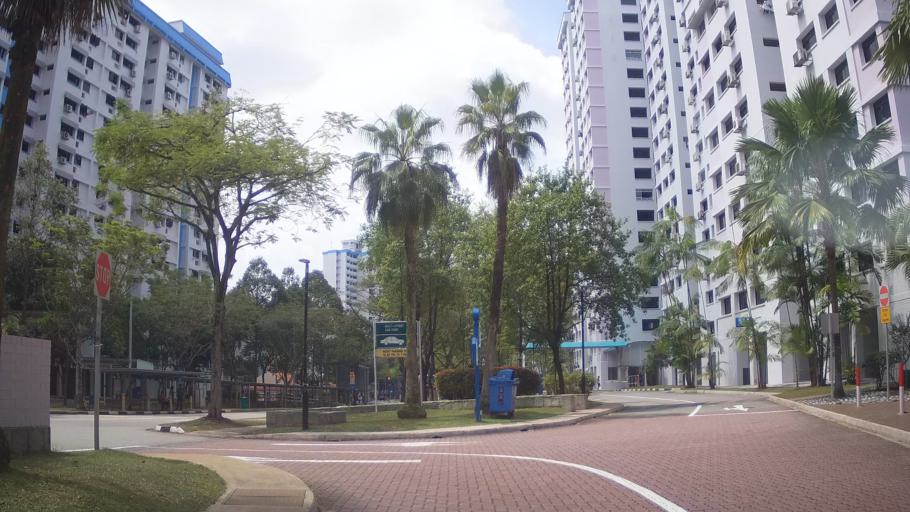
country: MY
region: Johor
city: Johor Bahru
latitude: 1.3878
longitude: 103.7678
